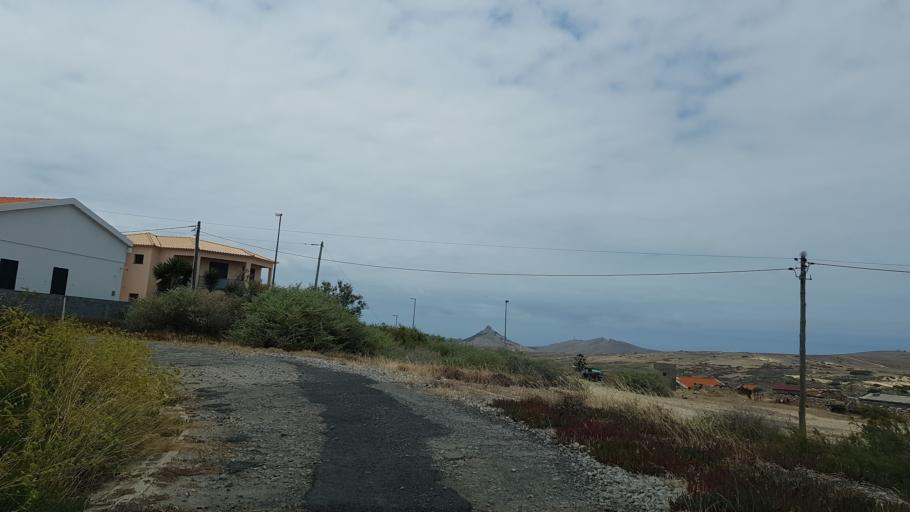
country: PT
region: Madeira
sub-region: Porto Santo
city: Camacha
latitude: 33.0883
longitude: -16.3412
